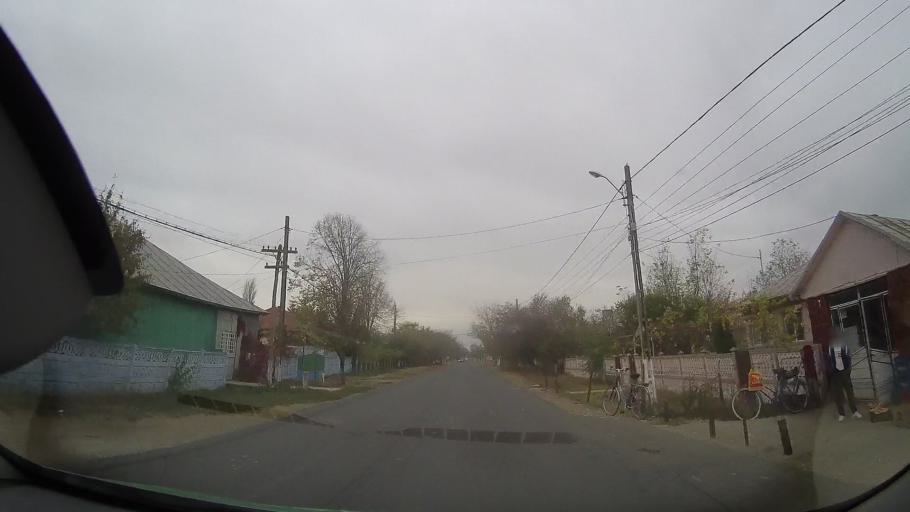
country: RO
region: Braila
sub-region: Comuna Ulmu
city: Ulmu
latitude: 44.9516
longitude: 27.3171
